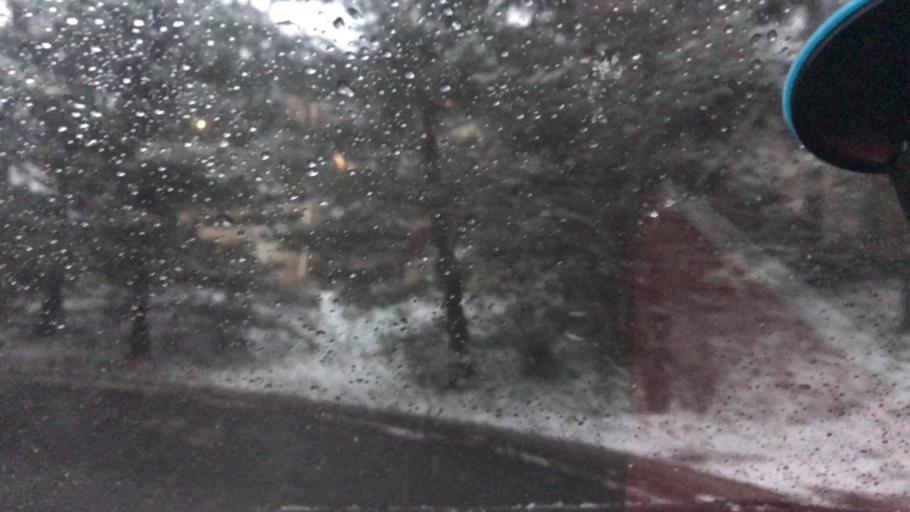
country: US
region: Maryland
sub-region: Prince George's County
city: Silver Hill
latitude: 38.8407
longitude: -76.9384
